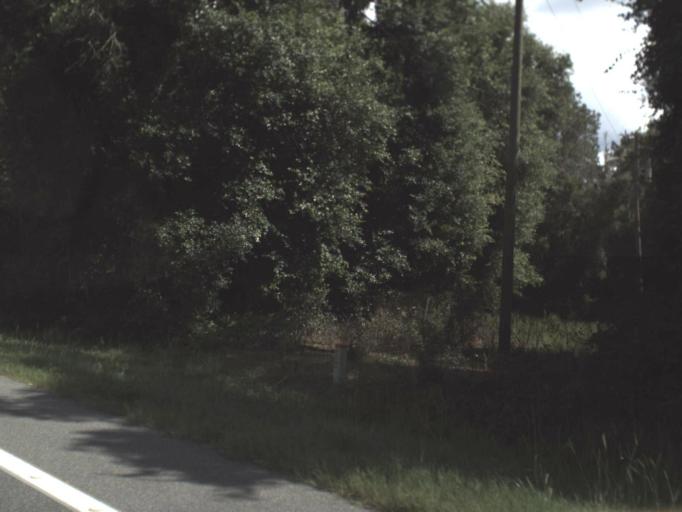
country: US
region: Florida
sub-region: Clay County
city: Keystone Heights
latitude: 29.7314
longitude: -81.9573
